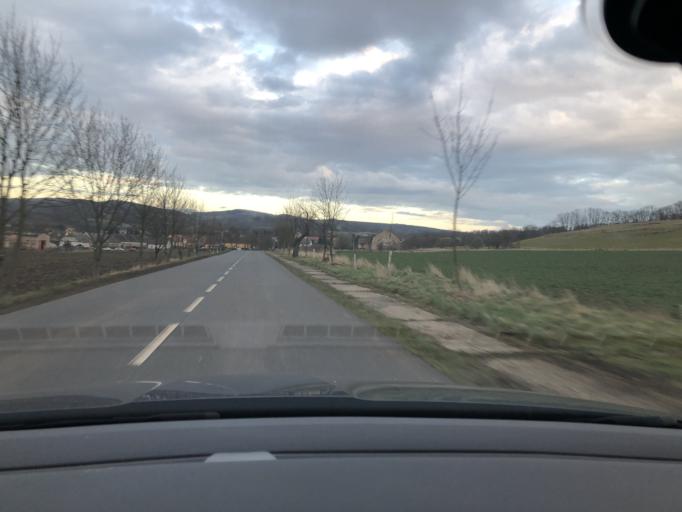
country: CZ
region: Ustecky
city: Rehlovice
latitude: 50.6065
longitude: 13.9438
